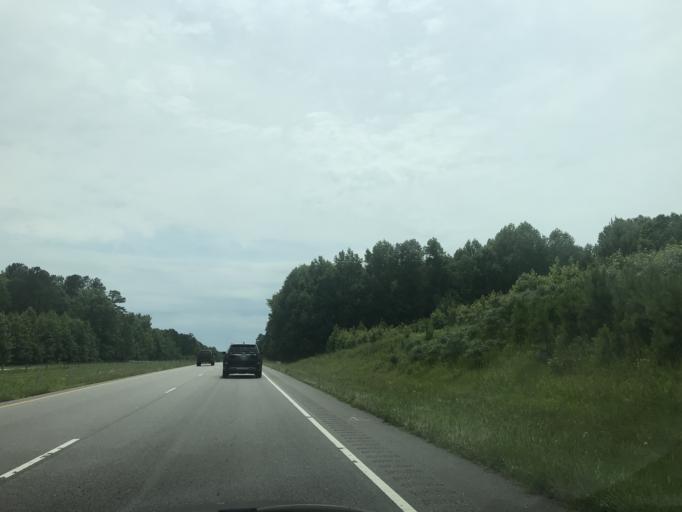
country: US
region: North Carolina
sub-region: Vance County
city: South Henderson
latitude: 36.2604
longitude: -78.4227
